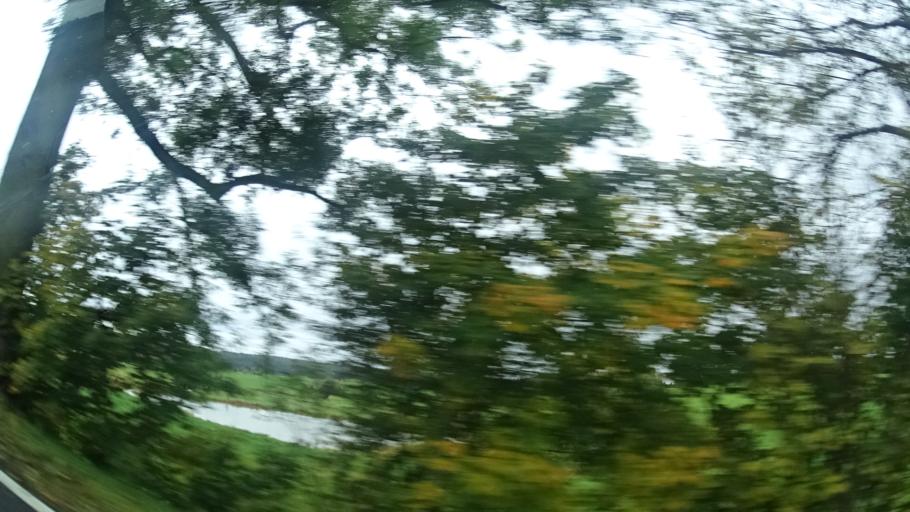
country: DE
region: Thuringia
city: Moxa
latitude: 50.6463
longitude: 11.6352
